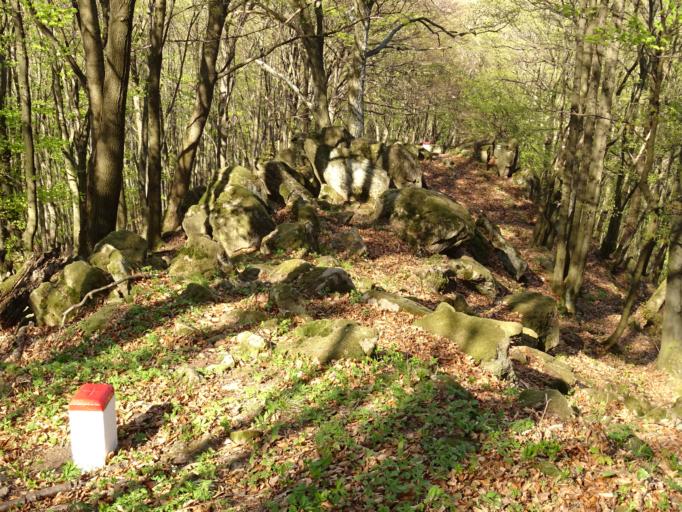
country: HU
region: Borsod-Abauj-Zemplen
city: Gonc
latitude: 48.5590
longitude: 21.3808
